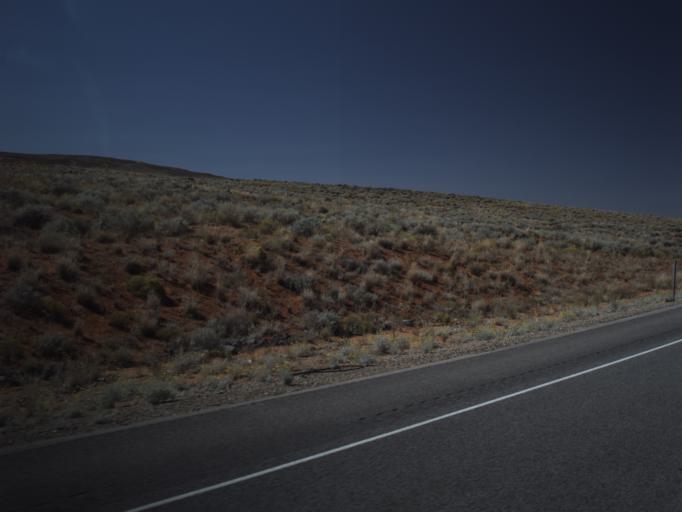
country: US
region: Utah
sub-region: Washington County
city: Washington
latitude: 37.1101
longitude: -113.4108
